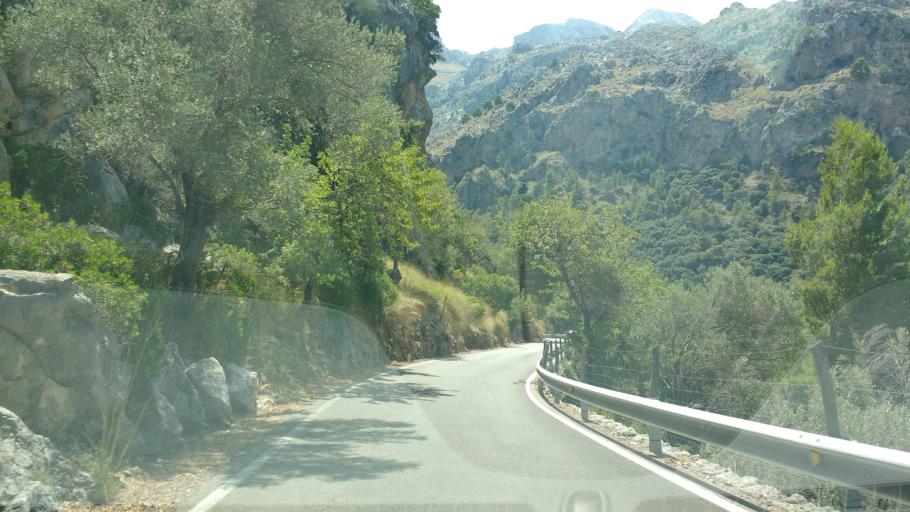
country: ES
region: Balearic Islands
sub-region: Illes Balears
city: Escorca
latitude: 39.8422
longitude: 2.7987
